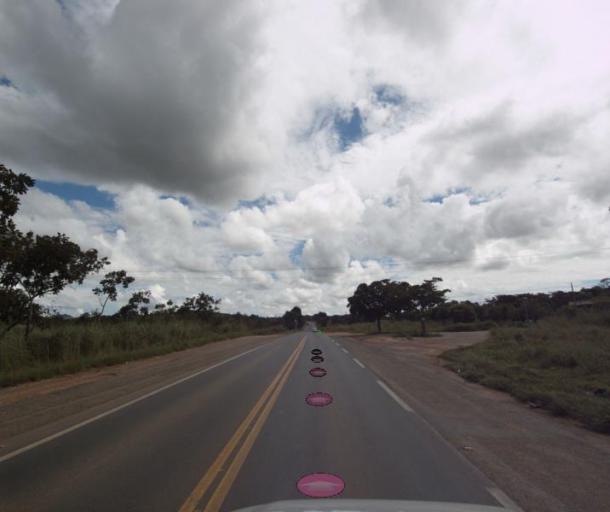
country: BR
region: Goias
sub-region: Uruacu
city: Uruacu
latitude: -14.4990
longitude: -49.1504
